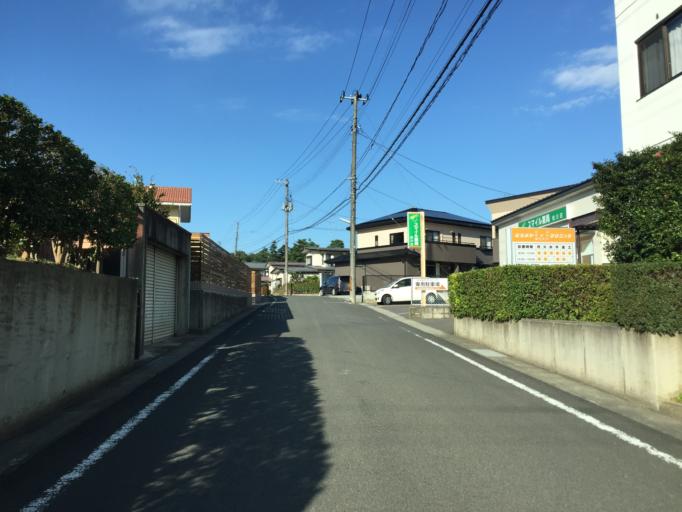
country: JP
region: Fukushima
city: Nihommatsu
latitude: 37.6553
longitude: 140.4862
